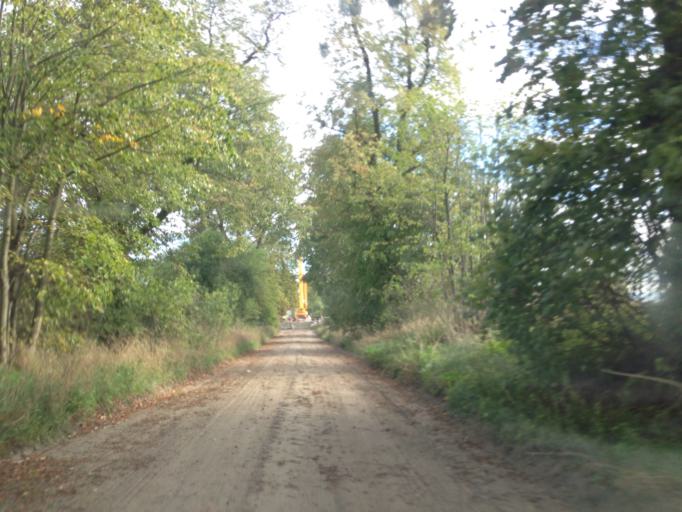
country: PL
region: Warmian-Masurian Voivodeship
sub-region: Powiat ilawski
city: Susz
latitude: 53.7442
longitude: 19.3139
